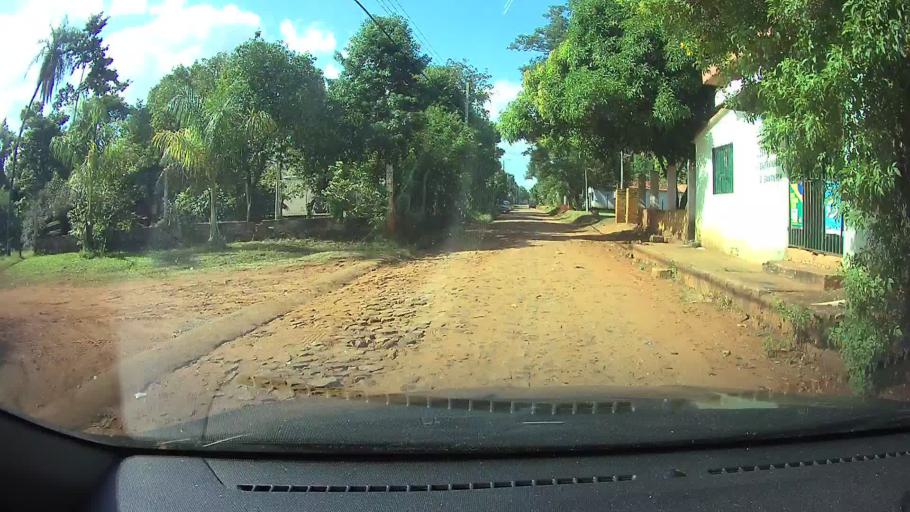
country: PY
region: Central
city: Limpio
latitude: -25.2451
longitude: -57.4675
